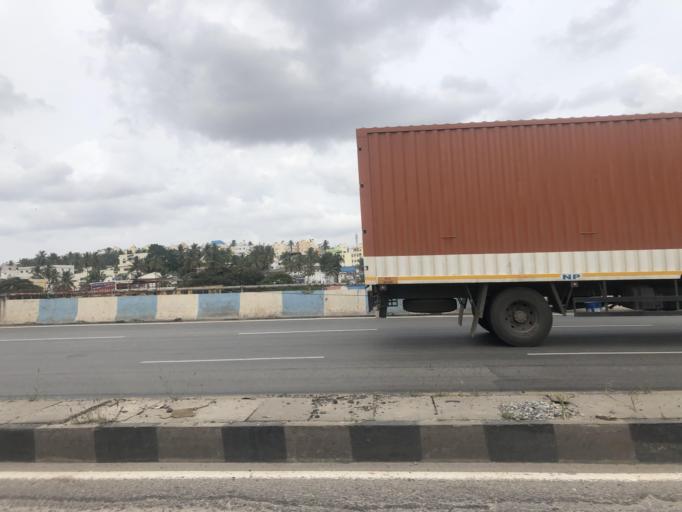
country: IN
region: Karnataka
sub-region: Bangalore Urban
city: Bangalore
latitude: 12.9866
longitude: 77.5191
